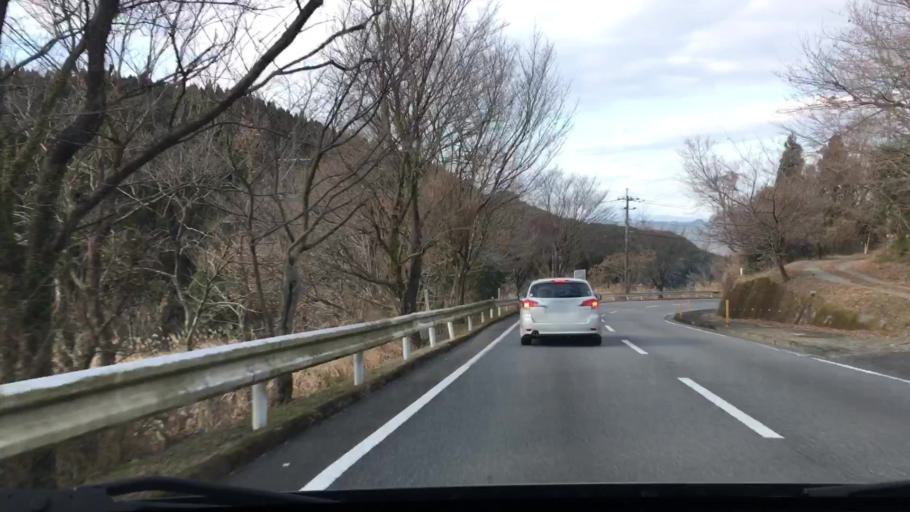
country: JP
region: Miyazaki
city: Miyazaki-shi
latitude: 31.8036
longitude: 131.3014
